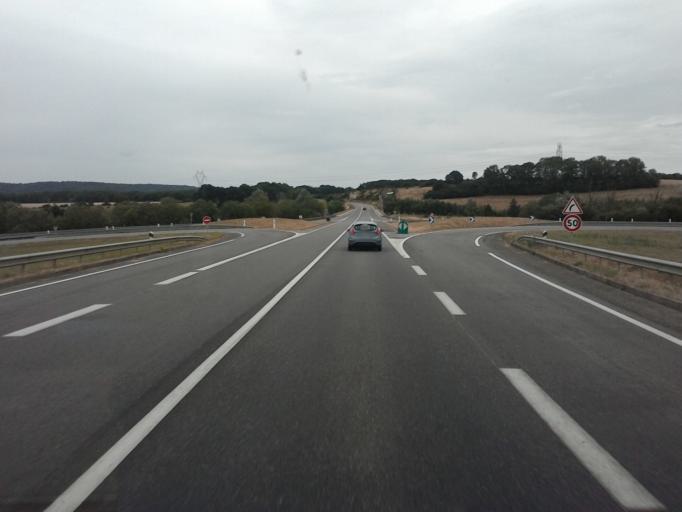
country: FR
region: Lorraine
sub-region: Departement de Meurthe-et-Moselle
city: Bainville-sur-Madon
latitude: 48.5817
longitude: 6.1026
